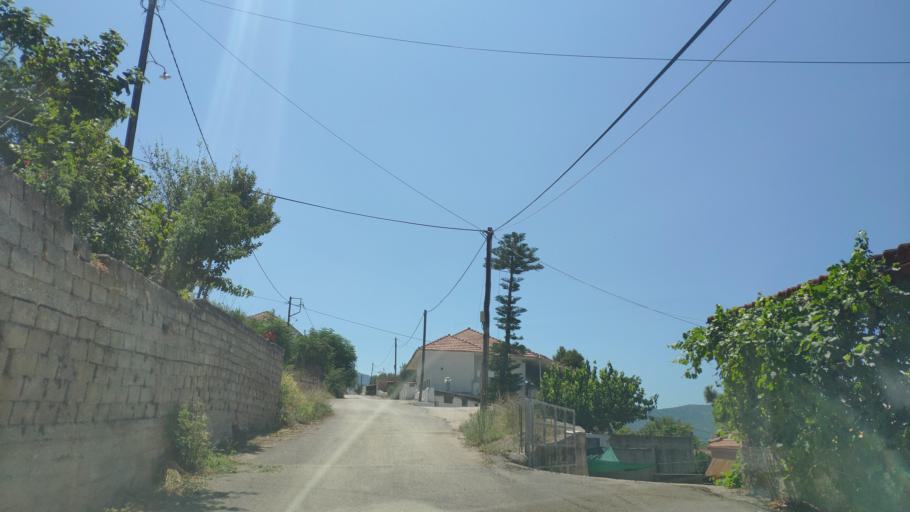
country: GR
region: Epirus
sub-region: Nomos Prevezis
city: Kanalaki
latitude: 39.2760
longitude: 20.5986
